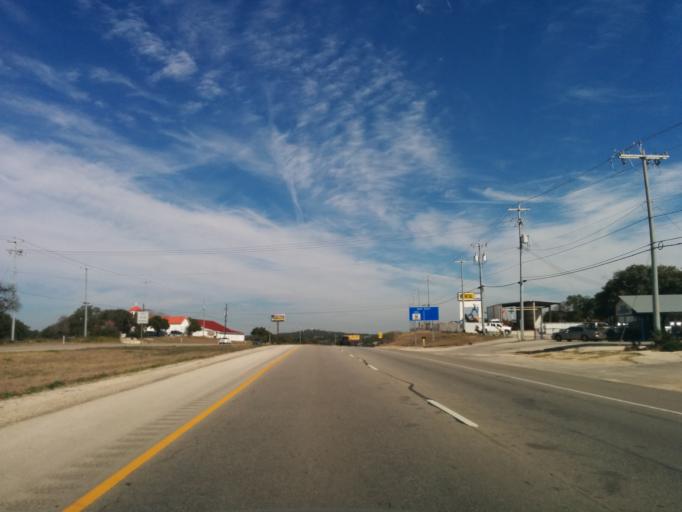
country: US
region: Texas
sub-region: Comal County
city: Bulverde
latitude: 29.7366
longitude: -98.4389
